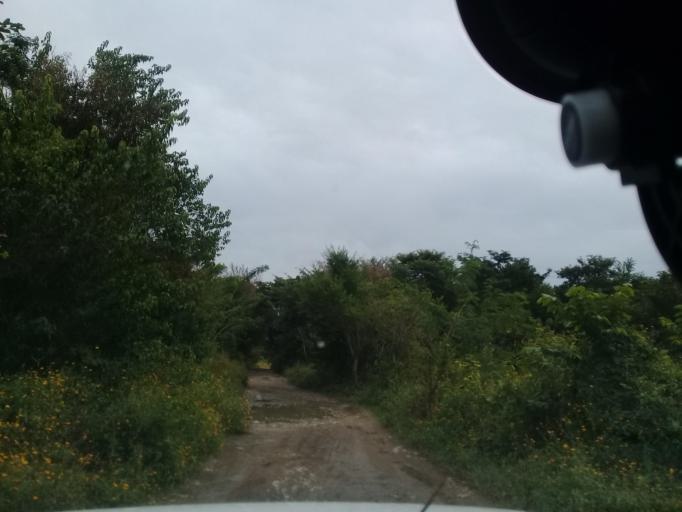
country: MX
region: Hidalgo
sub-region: Huejutla de Reyes
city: Chalahuiyapa
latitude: 21.1718
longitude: -98.3741
